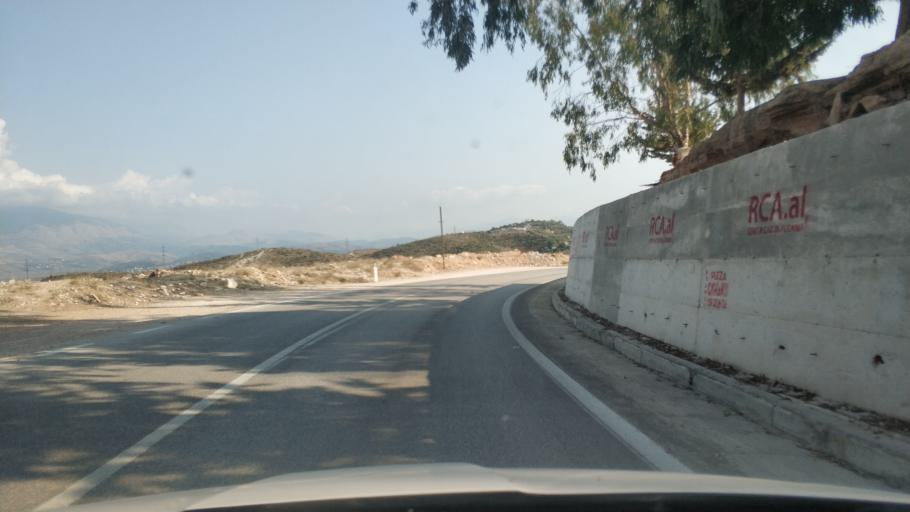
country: AL
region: Vlore
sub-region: Rrethi i Sarandes
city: Sarande
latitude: 39.8883
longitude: 20.0172
